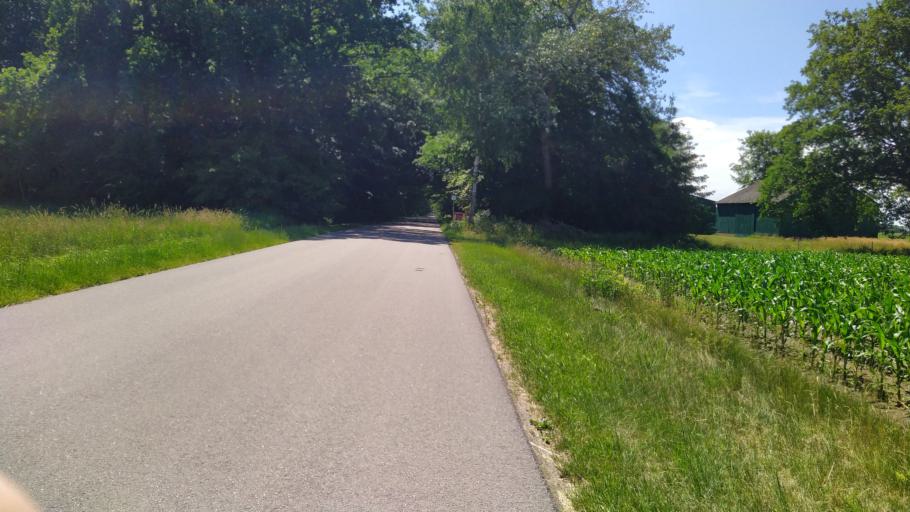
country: DE
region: Lower Saxony
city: Oldendorf
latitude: 53.5631
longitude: 9.2415
